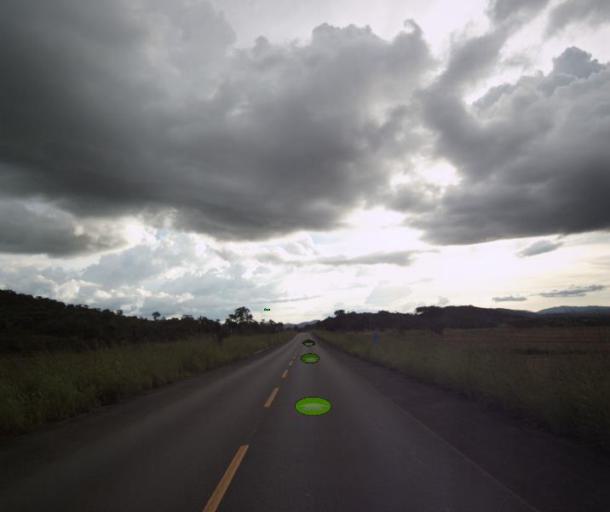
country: BR
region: Goias
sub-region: Niquelandia
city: Niquelandia
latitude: -14.5013
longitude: -48.5125
